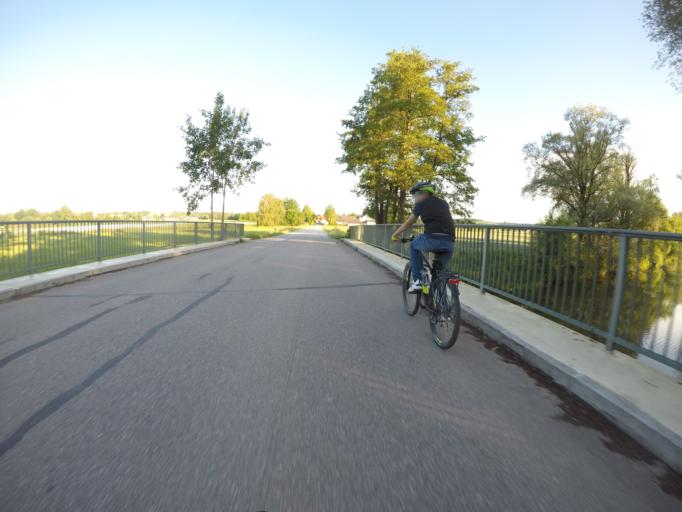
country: DE
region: Bavaria
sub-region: Lower Bavaria
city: Reisbach
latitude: 48.5805
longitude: 12.6223
